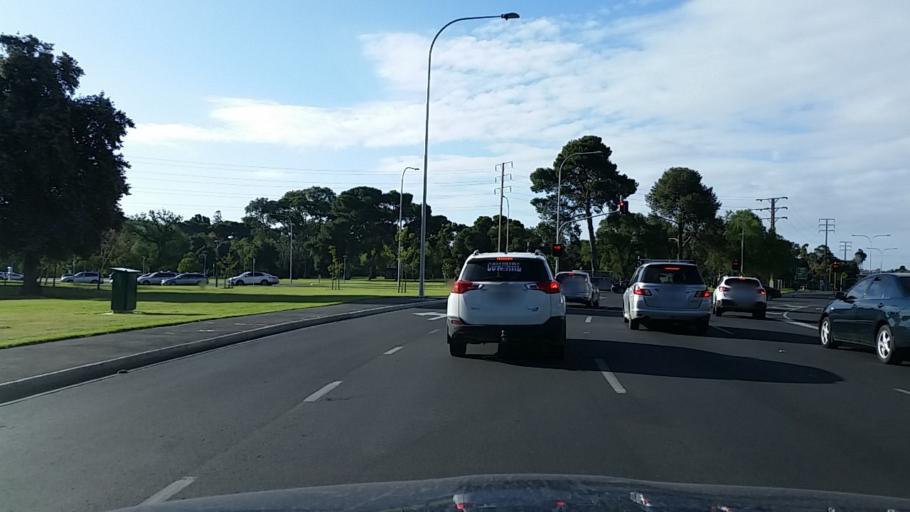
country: AU
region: South Australia
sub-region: Adelaide
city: Adelaide
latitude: -34.9227
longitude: 138.6158
